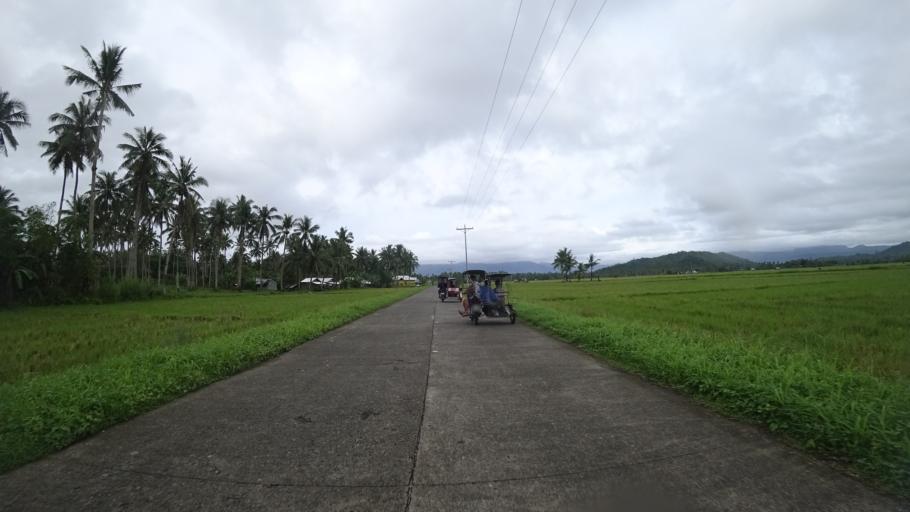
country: PH
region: Eastern Visayas
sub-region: Province of Leyte
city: MacArthur
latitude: 10.8184
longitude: 124.9808
